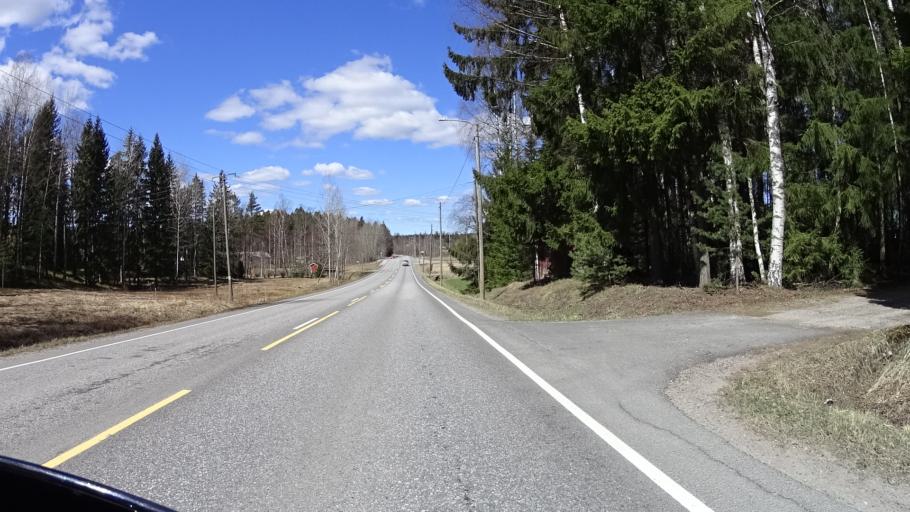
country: FI
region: Uusimaa
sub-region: Helsinki
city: Kirkkonummi
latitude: 60.2639
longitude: 24.4712
